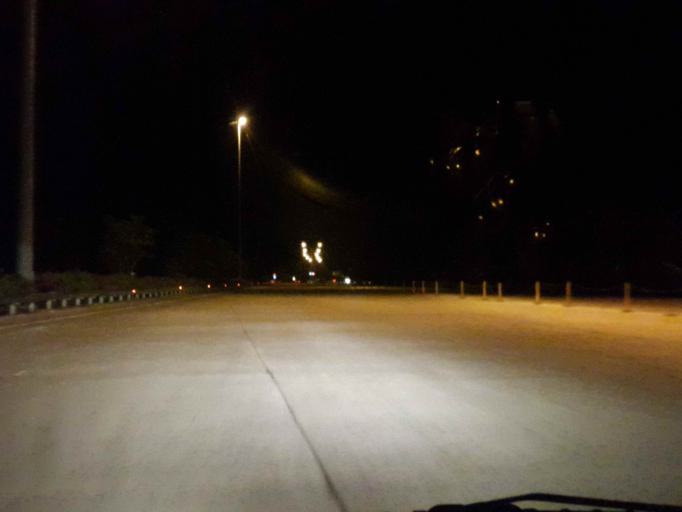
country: ID
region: West Java
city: Karangsembung
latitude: -6.8293
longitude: 108.6388
